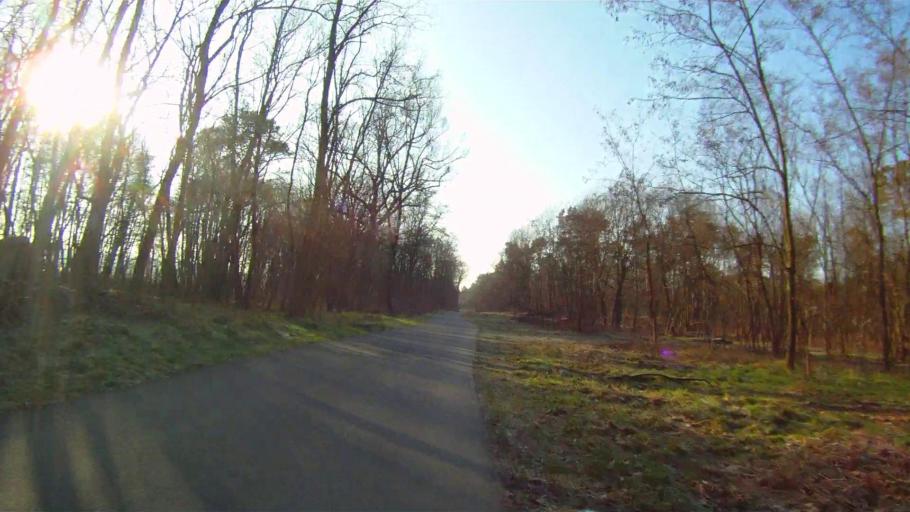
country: DE
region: Berlin
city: Friedrichshagen
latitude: 52.4375
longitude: 13.6198
